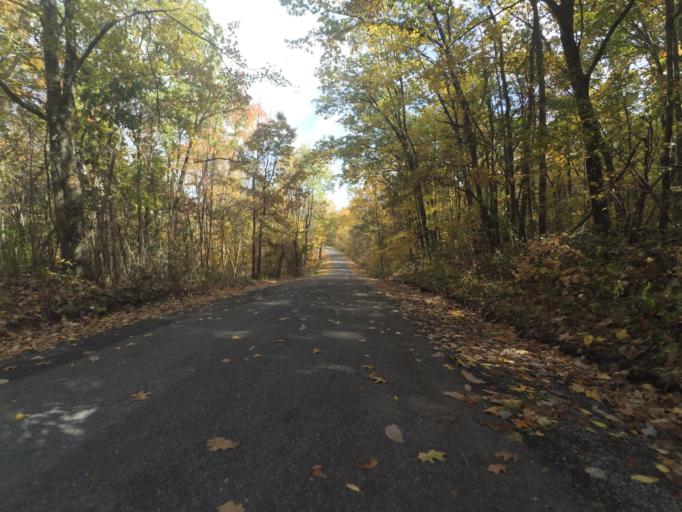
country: US
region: Pennsylvania
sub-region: Centre County
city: Park Forest Village
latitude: 40.8935
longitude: -77.9466
